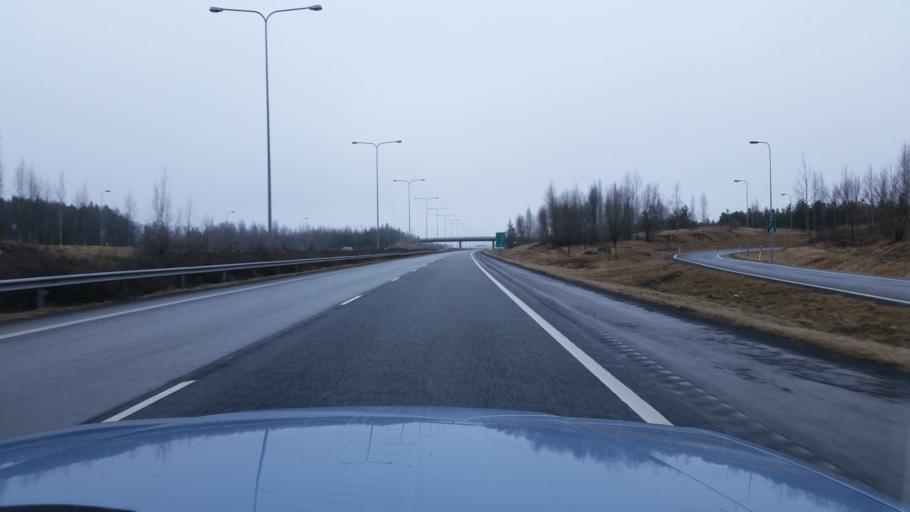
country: FI
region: Pirkanmaa
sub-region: Etelae-Pirkanmaa
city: Toijala
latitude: 61.2222
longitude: 23.8388
